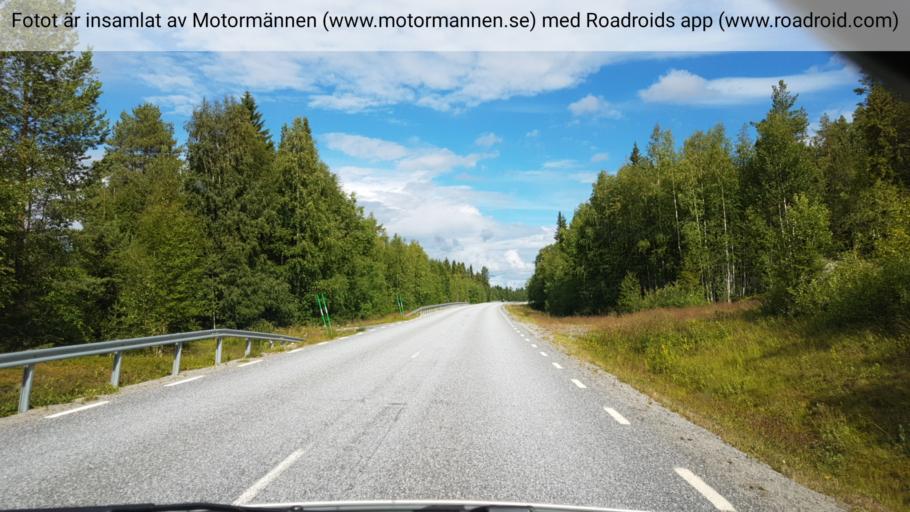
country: SE
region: Vaesterbotten
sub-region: Vilhelmina Kommun
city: Vilhelmina
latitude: 64.4232
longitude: 16.8052
